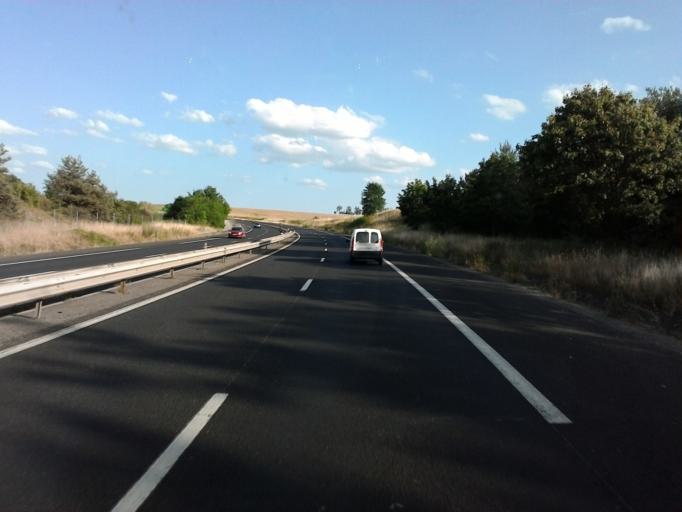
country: FR
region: Lorraine
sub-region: Departement de Meurthe-et-Moselle
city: Flavigny-sur-Moselle
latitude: 48.5639
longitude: 6.1763
